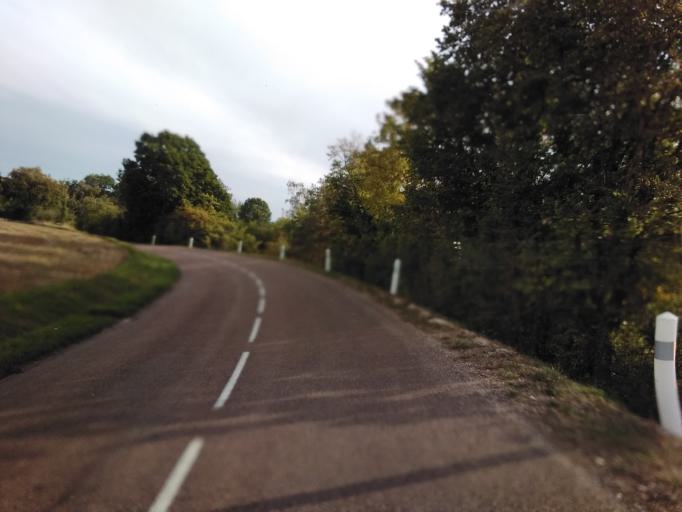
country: FR
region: Champagne-Ardenne
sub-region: Departement de l'Aube
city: Les Riceys
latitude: 47.8985
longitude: 4.3582
